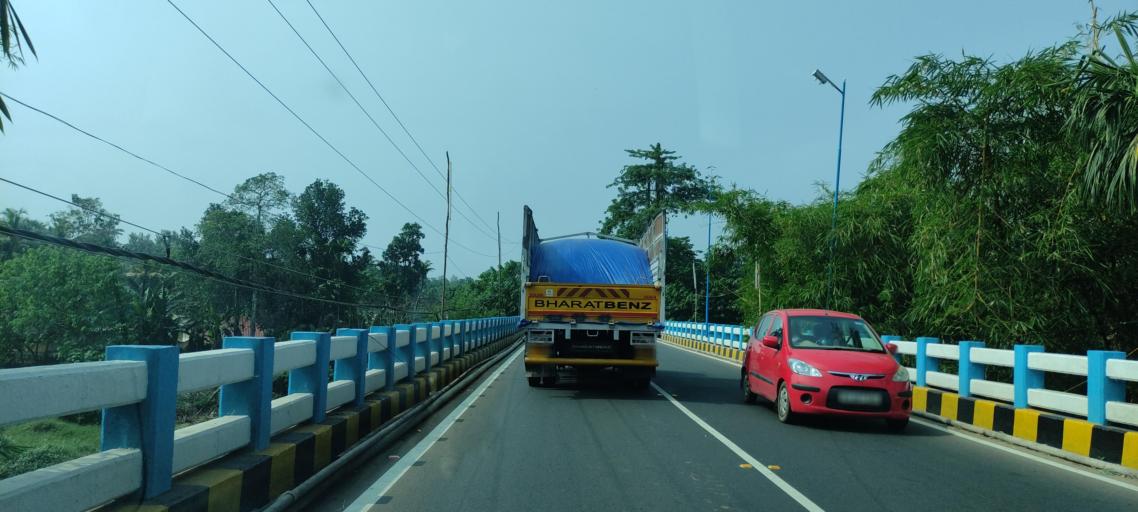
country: IN
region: Kerala
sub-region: Pattanamtitta
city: Adur
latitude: 9.2337
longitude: 76.6737
